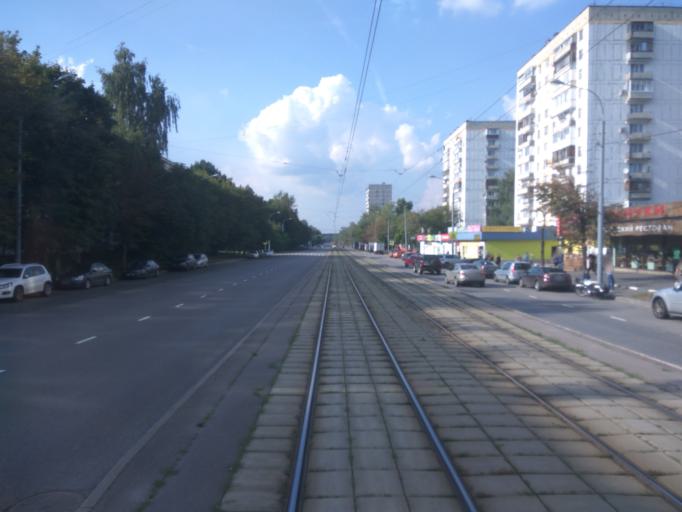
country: RU
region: Moscow
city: Perovo
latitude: 55.7532
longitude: 37.7911
